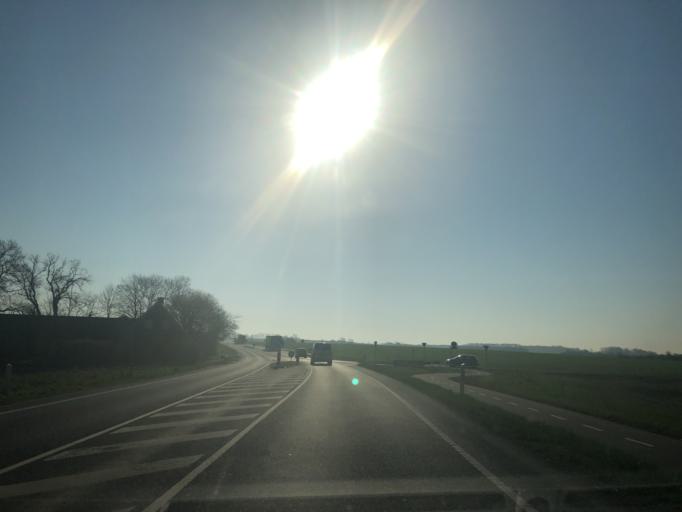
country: DK
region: Zealand
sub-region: Faxe Kommune
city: Ronnede
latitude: 55.2567
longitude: 12.0564
